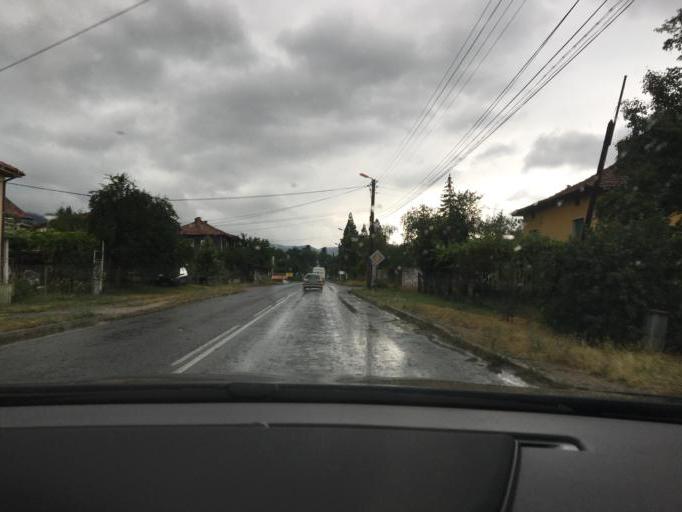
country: BG
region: Kyustendil
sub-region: Obshtina Kyustendil
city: Kyustendil
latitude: 42.2705
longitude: 22.6375
